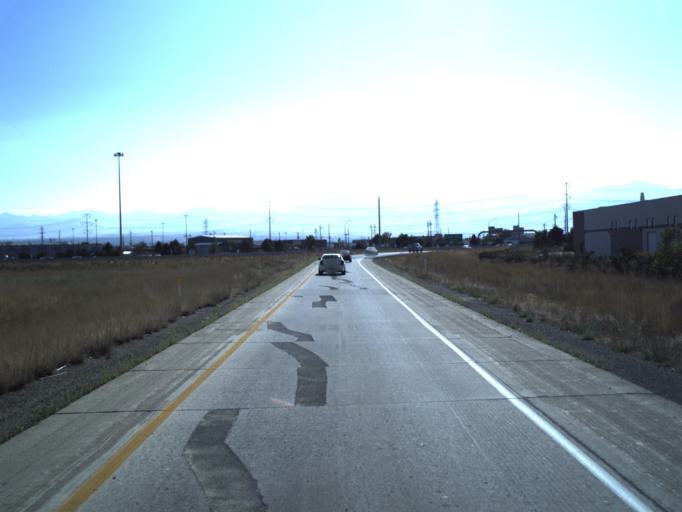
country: US
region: Utah
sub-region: Salt Lake County
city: West Valley City
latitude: 40.7272
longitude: -111.9529
